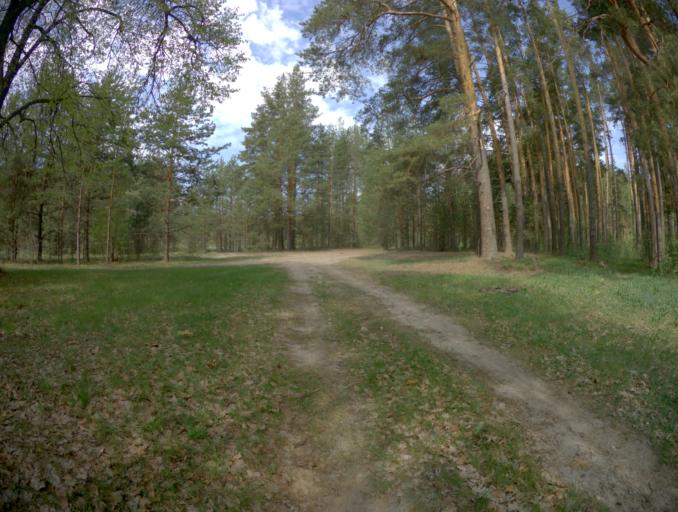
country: RU
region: Ivanovo
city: Yuzha
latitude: 56.4671
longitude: 42.1323
